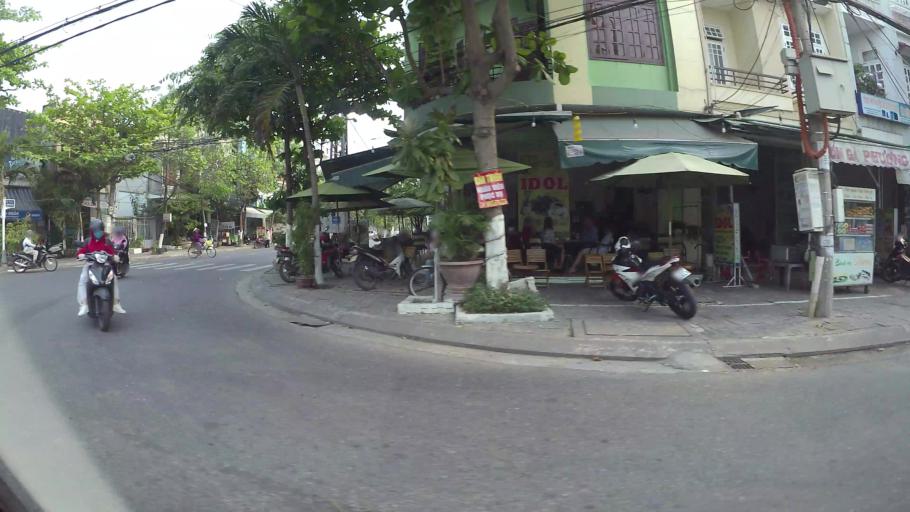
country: VN
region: Da Nang
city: Da Nang
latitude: 16.0443
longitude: 108.2131
